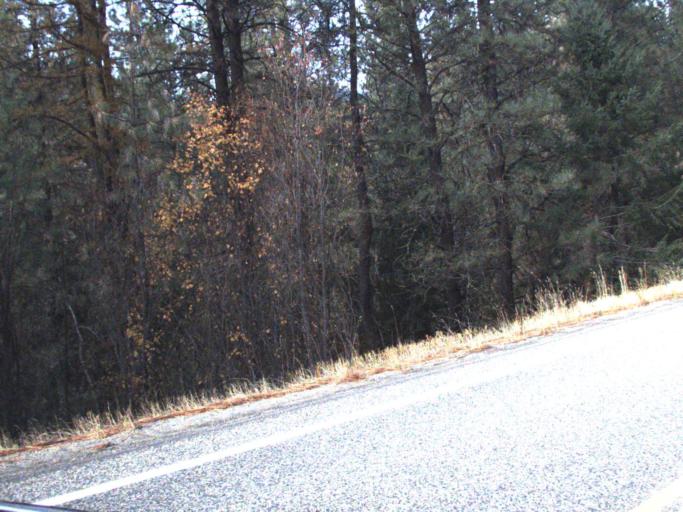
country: US
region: Washington
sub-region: Stevens County
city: Kettle Falls
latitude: 48.8064
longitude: -118.0015
